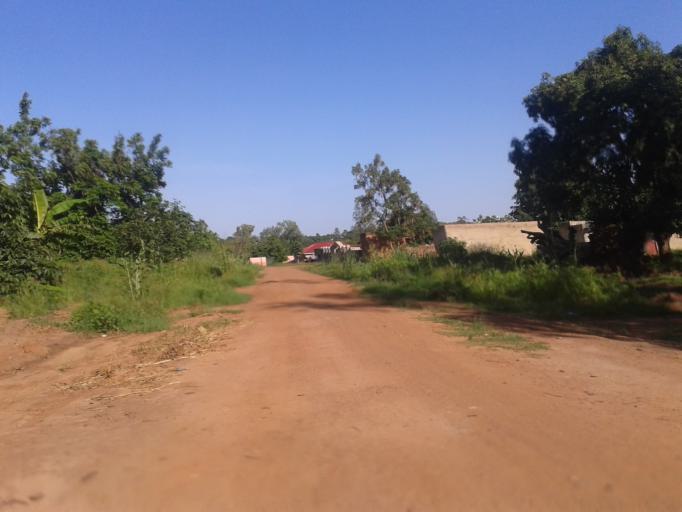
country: UG
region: Northern Region
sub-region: Gulu District
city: Gulu
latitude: 2.7903
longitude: 32.3124
